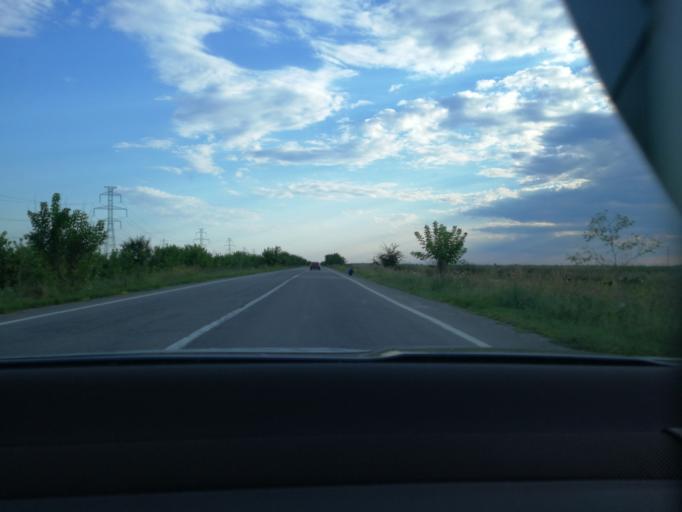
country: RO
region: Prahova
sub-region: Comuna Targsoru Vechi
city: Strejnicu
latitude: 44.8935
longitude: 25.9630
